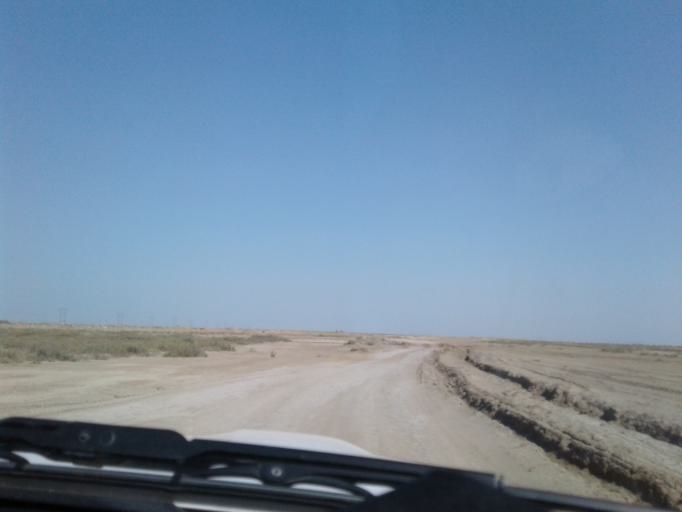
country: IR
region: Golestan
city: Gomishan
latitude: 37.8216
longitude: 53.9221
